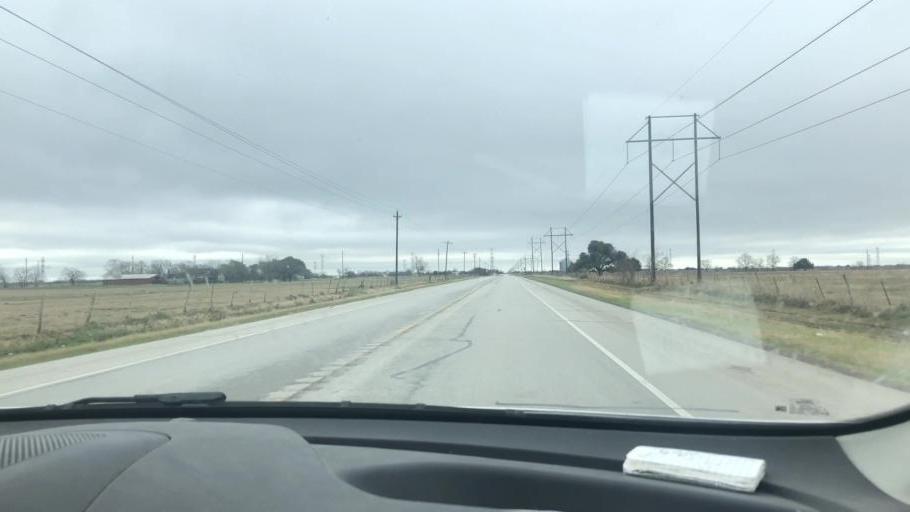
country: US
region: Texas
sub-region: Wharton County
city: Boling
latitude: 29.1851
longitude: -96.0110
